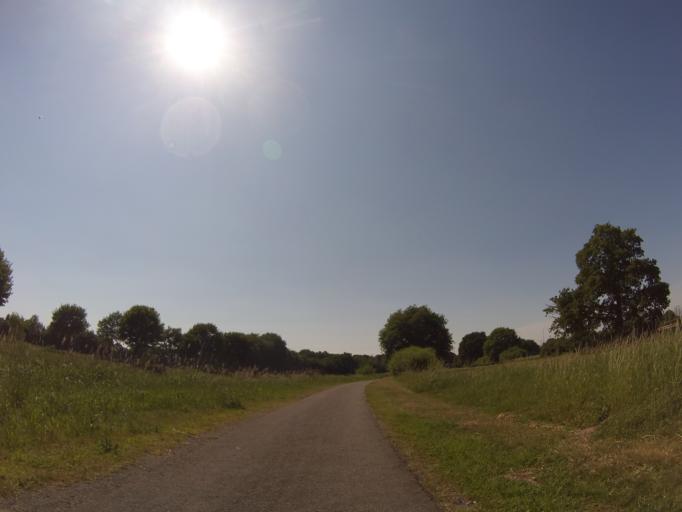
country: DE
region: Lower Saxony
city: Emlichheim
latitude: 52.6002
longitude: 6.8508
